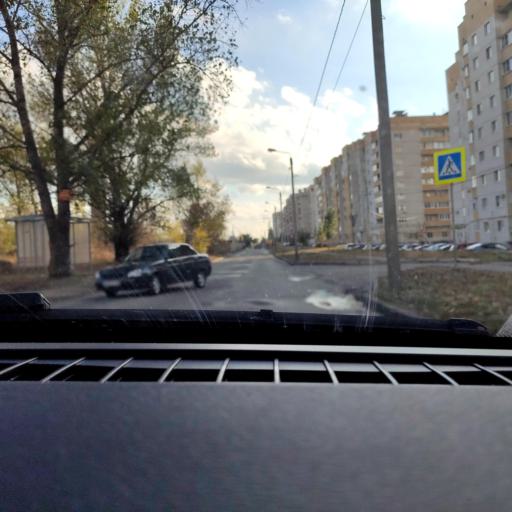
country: RU
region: Voronezj
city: Somovo
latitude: 51.6753
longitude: 39.2913
